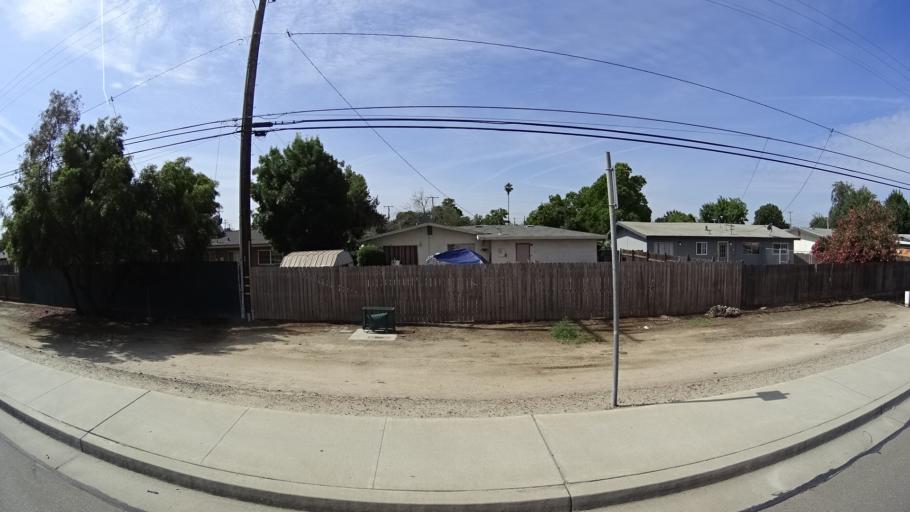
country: US
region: California
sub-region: Kings County
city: Hanford
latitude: 36.3425
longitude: -119.6627
